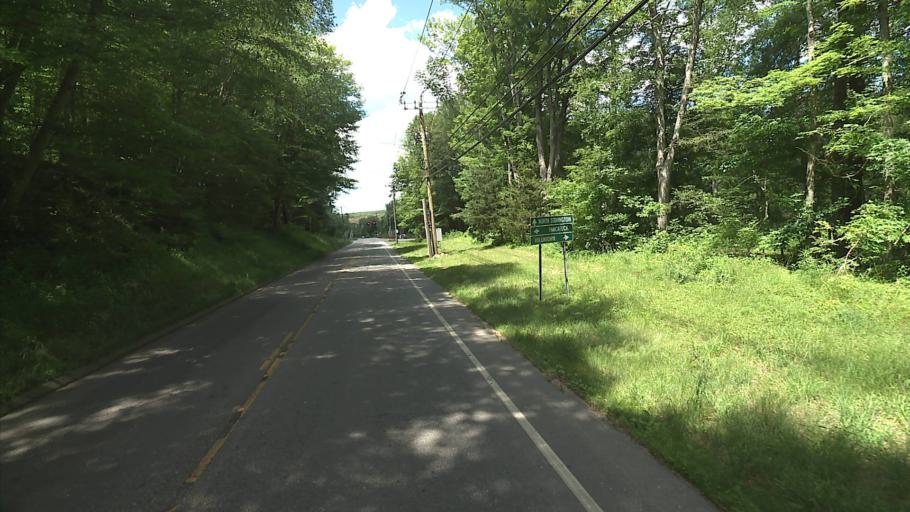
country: US
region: Connecticut
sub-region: New London County
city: Pawcatuck
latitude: 41.4321
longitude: -71.8464
